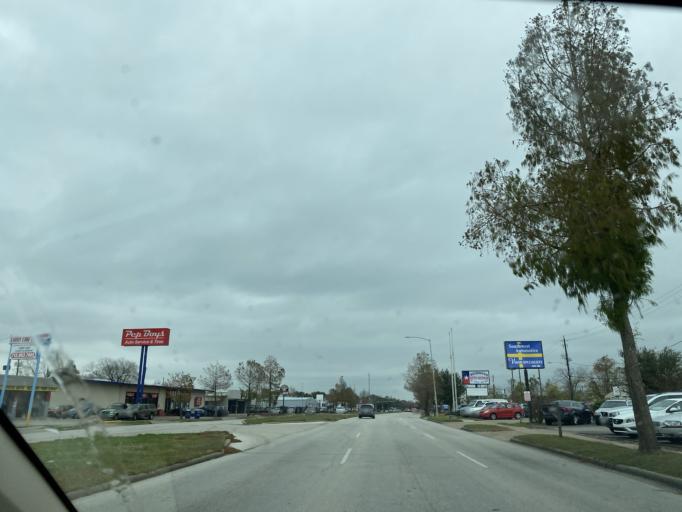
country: US
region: Texas
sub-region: Harris County
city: Piney Point Village
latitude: 29.7292
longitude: -95.5181
